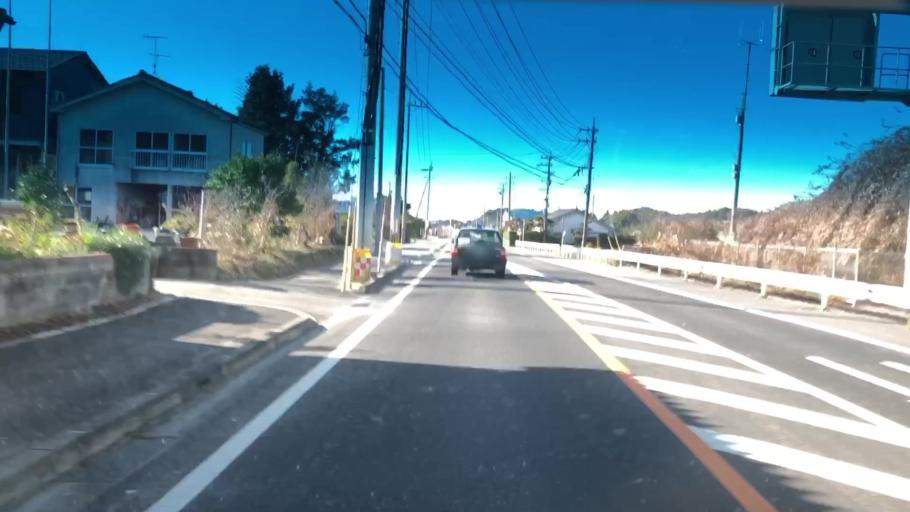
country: JP
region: Kagoshima
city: Satsumasendai
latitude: 31.8218
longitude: 130.2599
